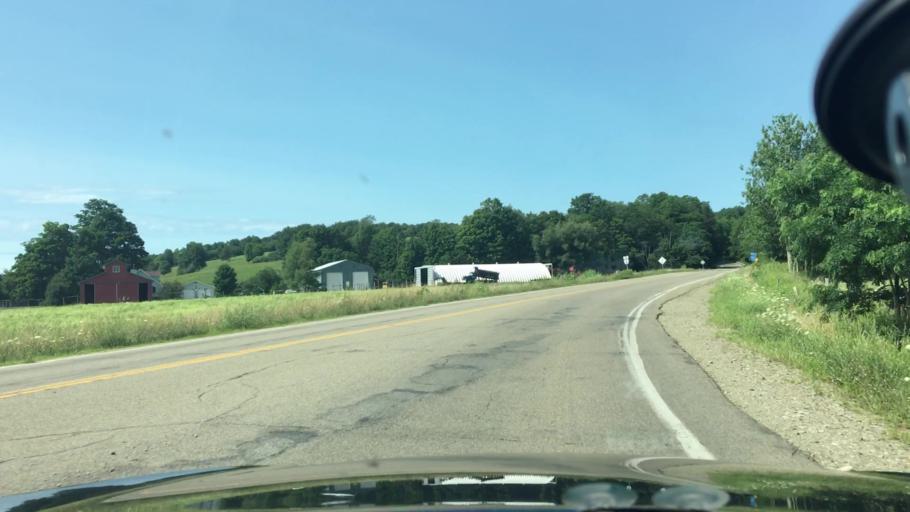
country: US
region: New York
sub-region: Chautauqua County
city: Brocton
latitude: 42.3370
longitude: -79.3668
